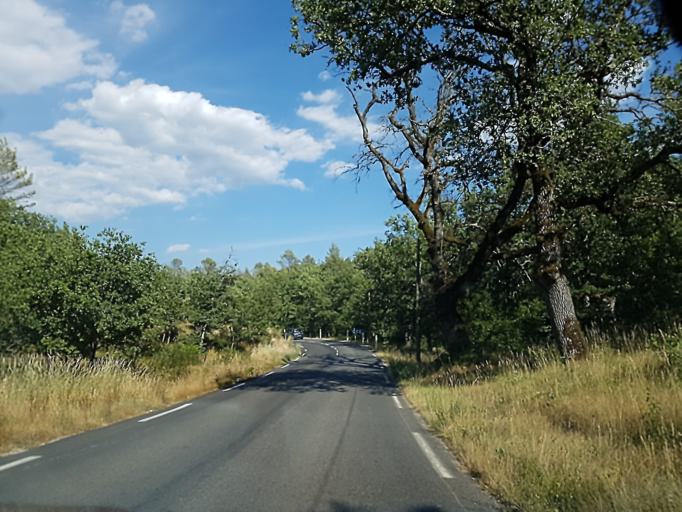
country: FR
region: Provence-Alpes-Cote d'Azur
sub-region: Departement du Var
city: Bras
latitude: 43.4596
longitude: 5.9199
